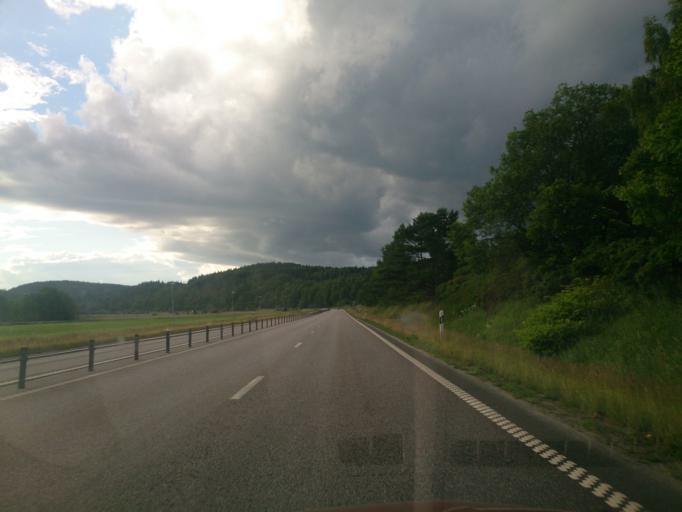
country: SE
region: OEstergoetland
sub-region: Norrkopings Kommun
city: Jursla
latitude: 58.6626
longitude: 16.1681
